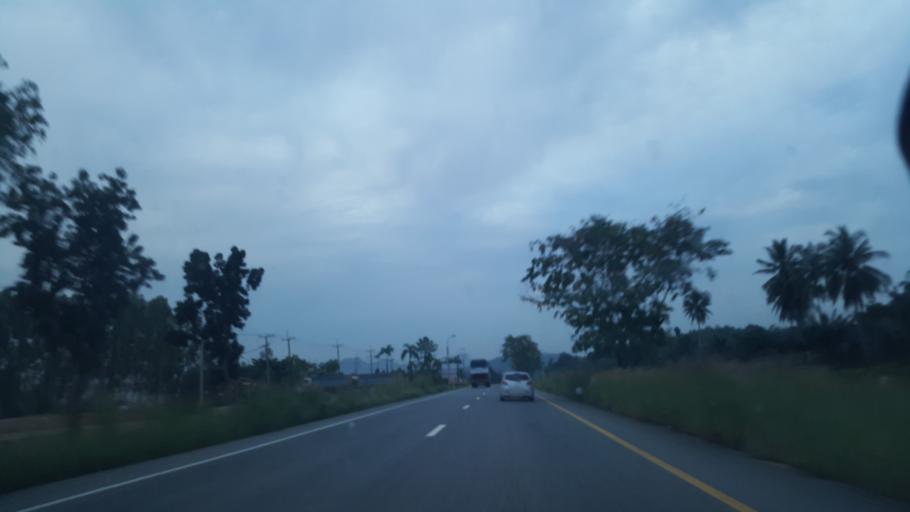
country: TH
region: Rayong
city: Ban Chang
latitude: 12.8317
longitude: 101.0058
